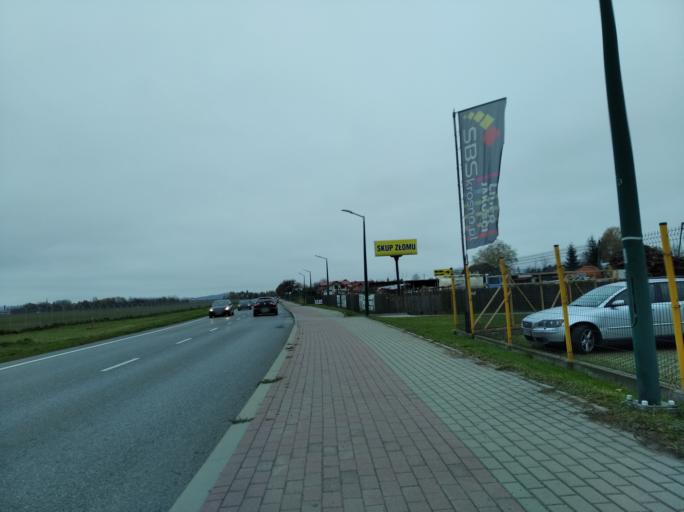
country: PL
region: Subcarpathian Voivodeship
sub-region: Krosno
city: Krosno
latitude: 49.6886
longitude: 21.7251
